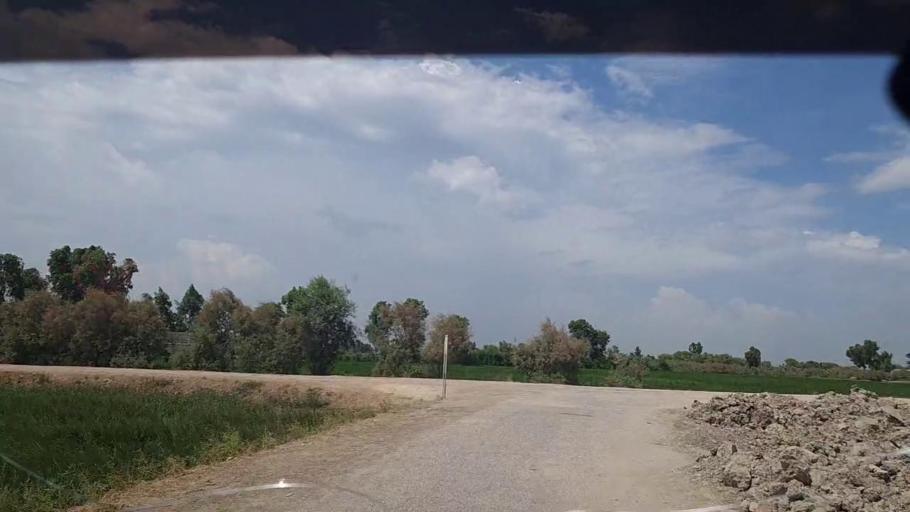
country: PK
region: Sindh
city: Ghauspur
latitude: 28.1547
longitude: 68.9971
